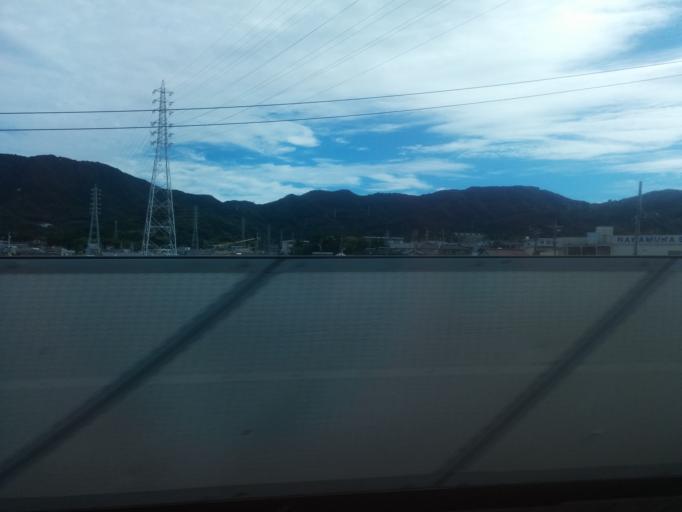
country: JP
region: Aichi
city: Gamagori
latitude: 34.8228
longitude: 137.2464
